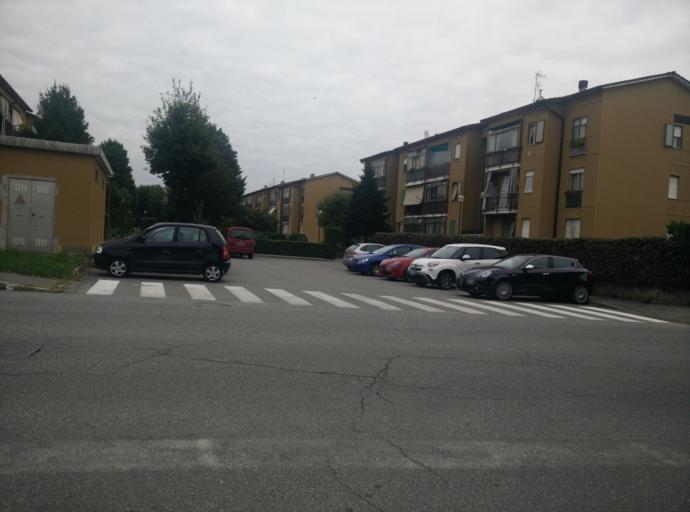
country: IT
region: Piedmont
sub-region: Provincia di Torino
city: Rivalta di Torino
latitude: 45.0244
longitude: 7.5209
